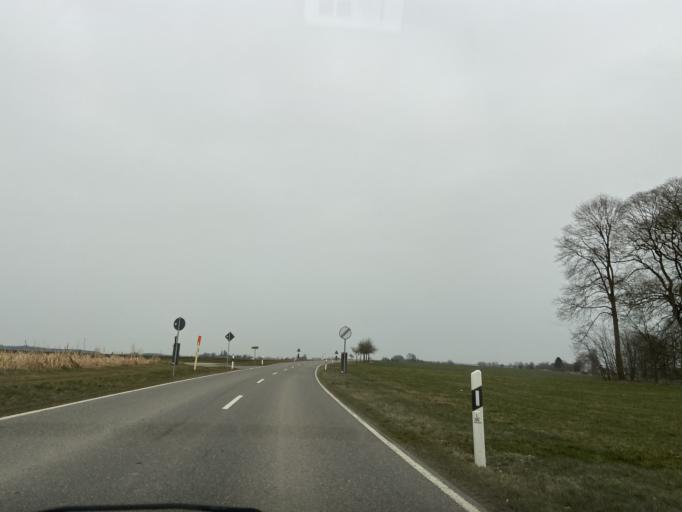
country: DE
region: Baden-Wuerttemberg
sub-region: Tuebingen Region
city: Ostrach
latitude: 47.9229
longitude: 9.3424
